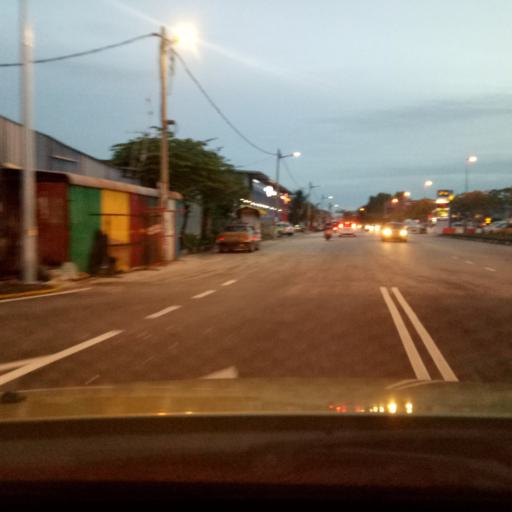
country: MY
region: Kedah
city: Alor Setar
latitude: 6.0932
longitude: 100.3838
